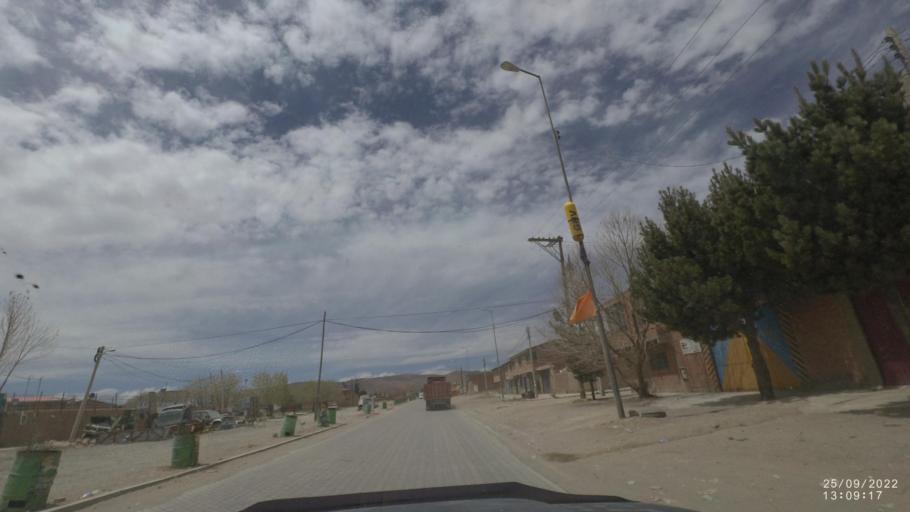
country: BO
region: Oruro
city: Oruro
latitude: -17.9757
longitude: -67.0574
